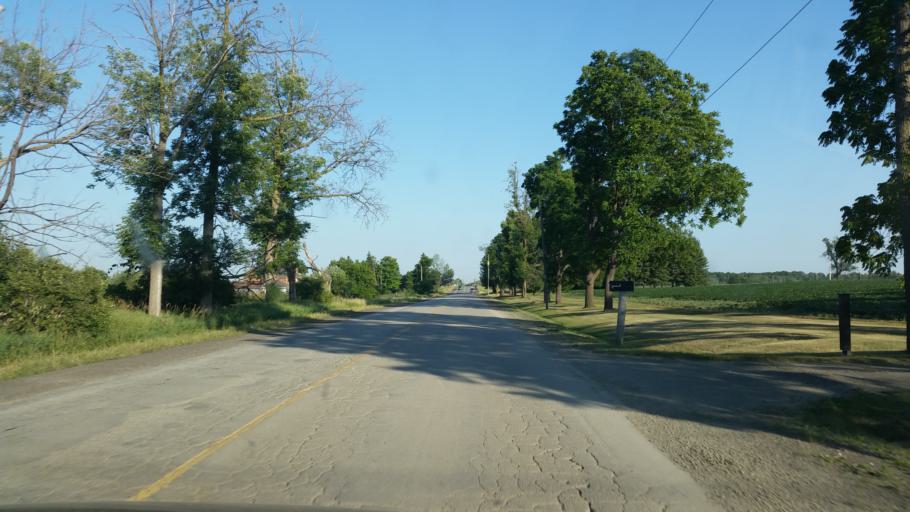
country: CA
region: Ontario
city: Brampton
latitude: 43.7584
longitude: -79.8111
